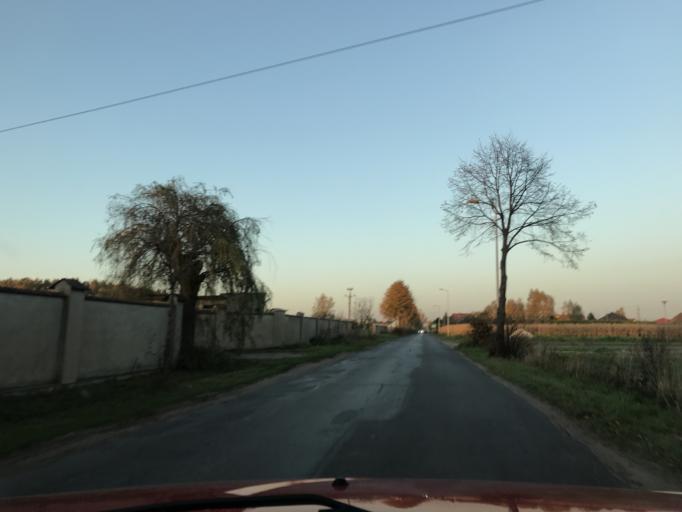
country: PL
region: Greater Poland Voivodeship
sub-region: Powiat poznanski
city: Baranowo
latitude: 52.3931
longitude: 16.7510
